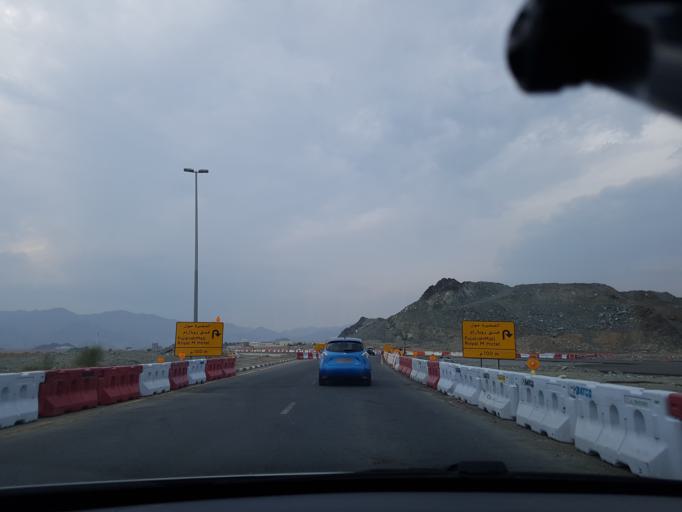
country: AE
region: Al Fujayrah
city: Al Fujayrah
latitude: 25.1218
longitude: 56.3145
